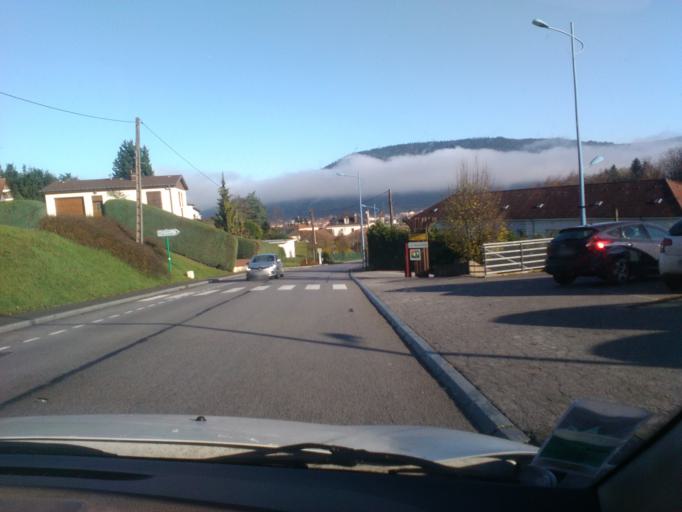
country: FR
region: Lorraine
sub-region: Departement des Vosges
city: Remiremont
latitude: 48.0092
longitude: 6.5819
